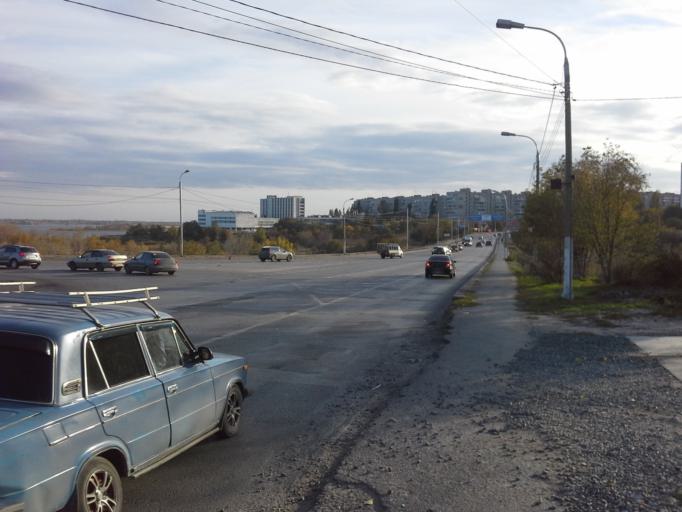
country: RU
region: Volgograd
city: Vodstroy
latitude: 48.8275
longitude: 44.6429
